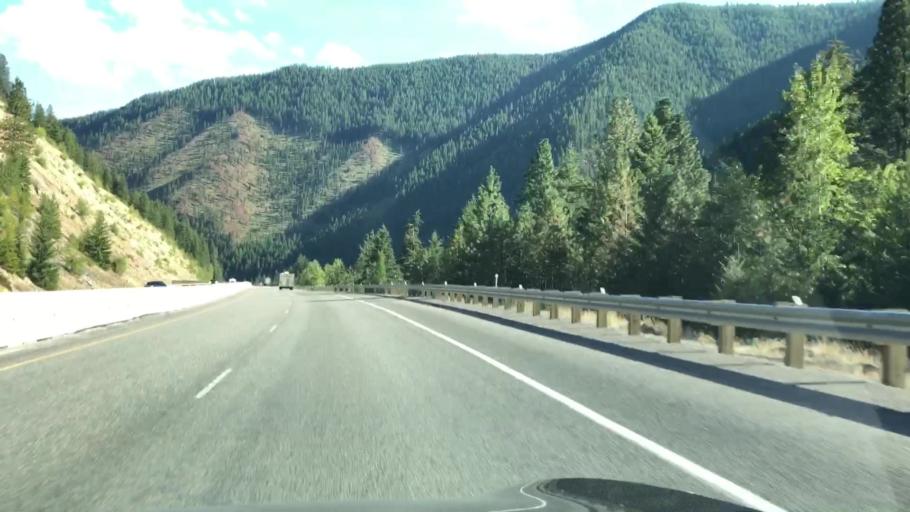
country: US
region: Montana
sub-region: Sanders County
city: Thompson Falls
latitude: 47.3084
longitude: -115.2077
